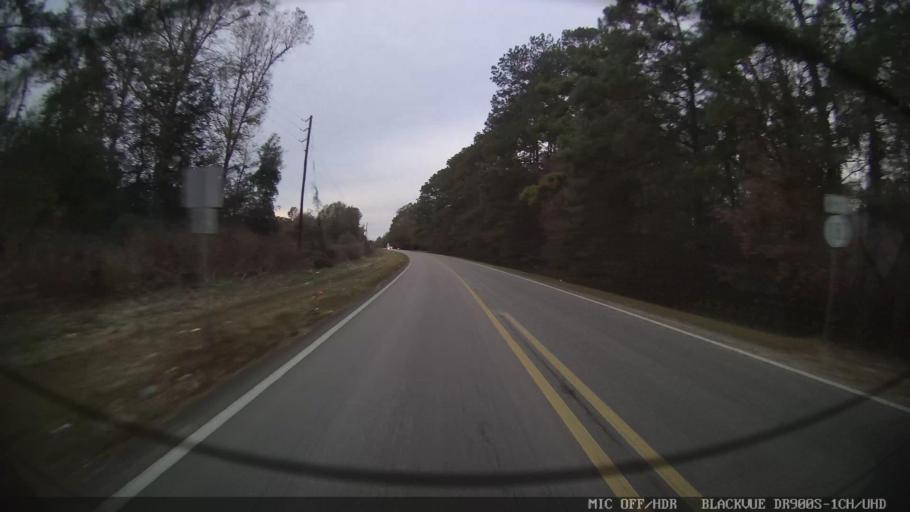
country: US
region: Mississippi
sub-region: Clarke County
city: Stonewall
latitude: 32.0234
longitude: -88.8528
